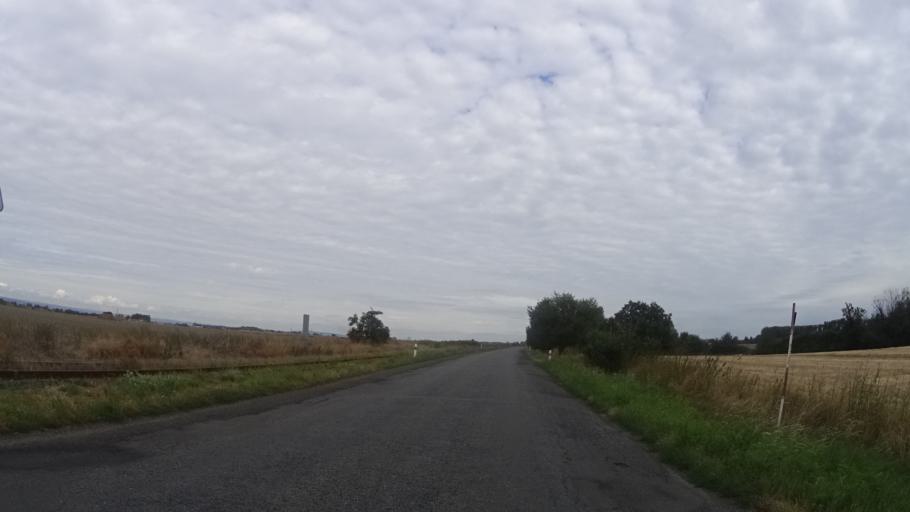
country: CZ
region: Olomoucky
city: Tovacov
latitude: 49.4066
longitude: 17.2848
